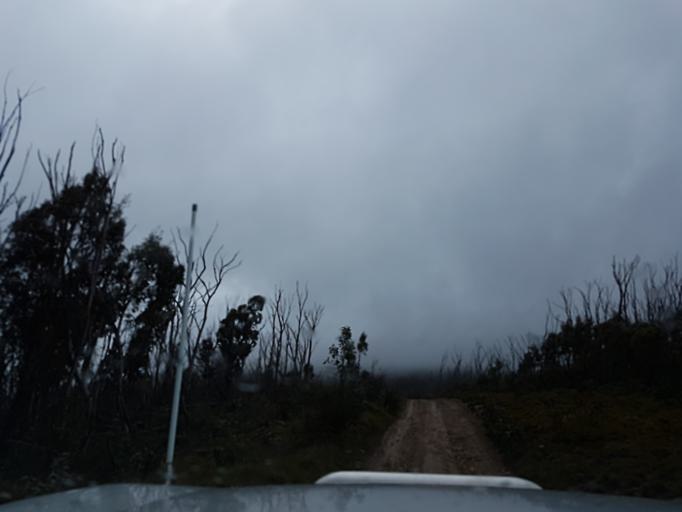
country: AU
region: Victoria
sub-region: Alpine
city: Mount Beauty
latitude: -37.0916
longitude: 147.0966
